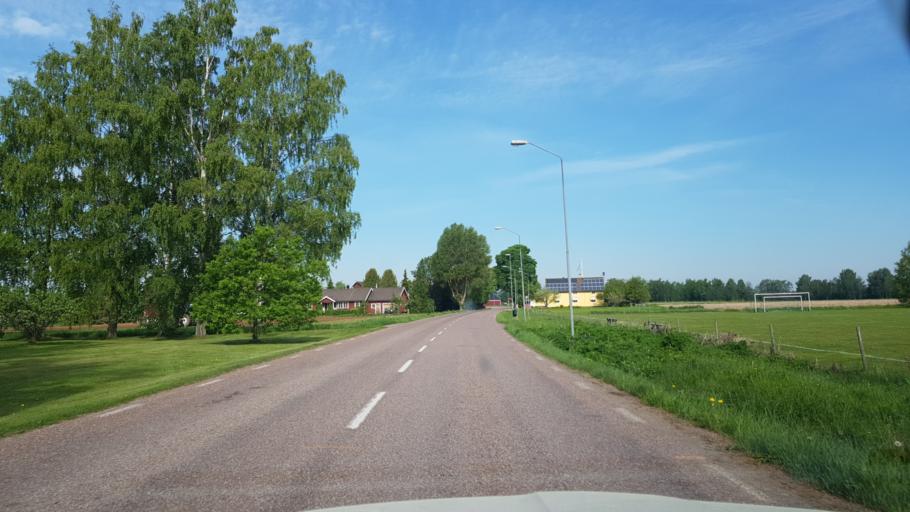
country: SE
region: Dalarna
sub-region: Borlange Kommun
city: Ornas
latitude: 60.4152
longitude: 15.5921
